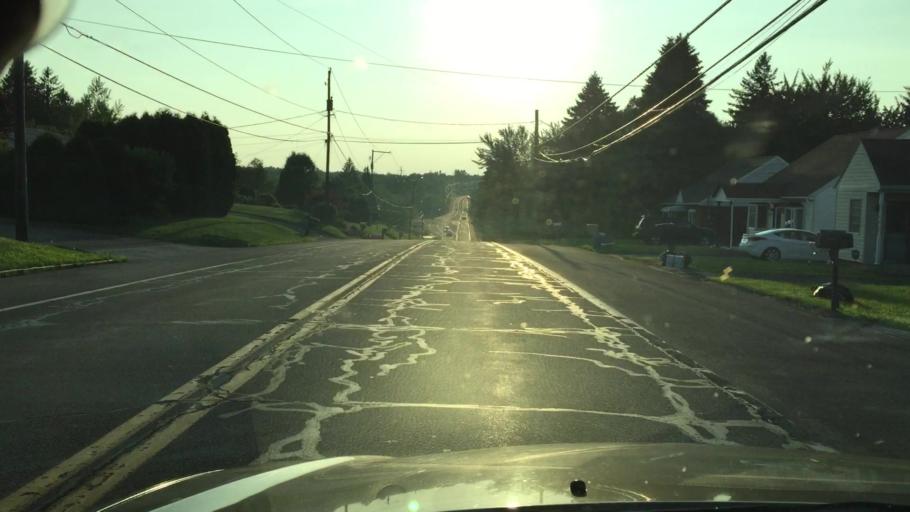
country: US
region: Pennsylvania
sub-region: Luzerne County
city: Hazleton
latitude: 40.9393
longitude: -75.9410
